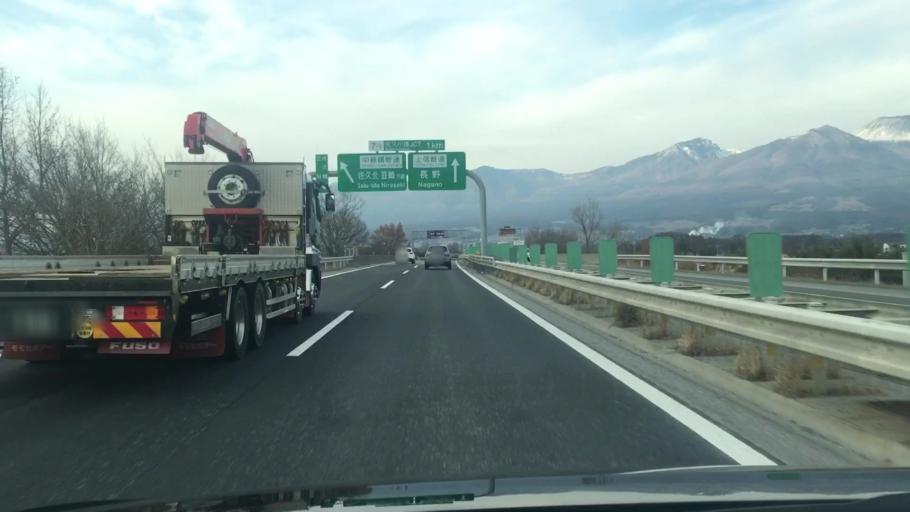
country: JP
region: Nagano
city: Komoro
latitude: 36.2907
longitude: 138.4822
